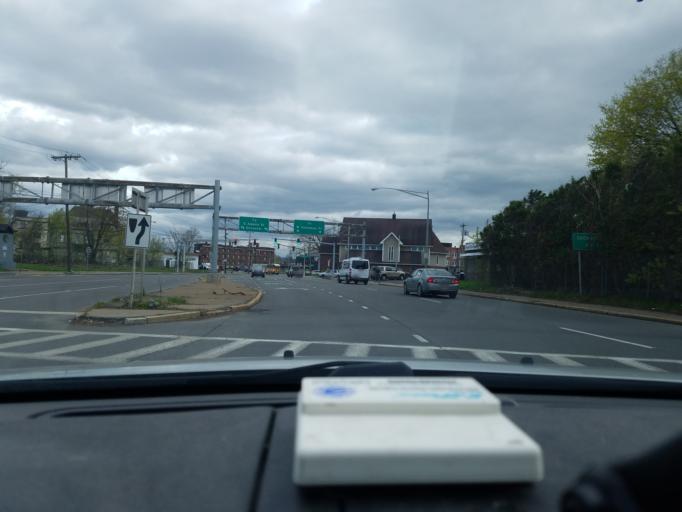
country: US
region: New York
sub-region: Onondaga County
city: Syracuse
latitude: 43.0426
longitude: -76.1580
